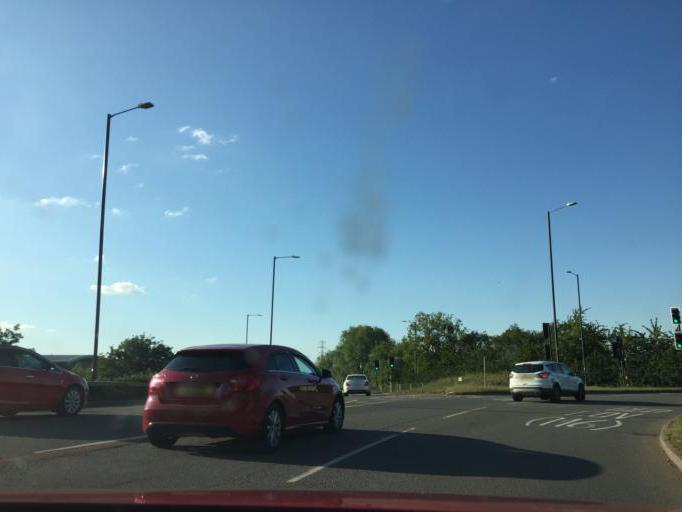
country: GB
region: England
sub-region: Warwickshire
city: Bedworth
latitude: 52.4987
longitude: -1.4740
